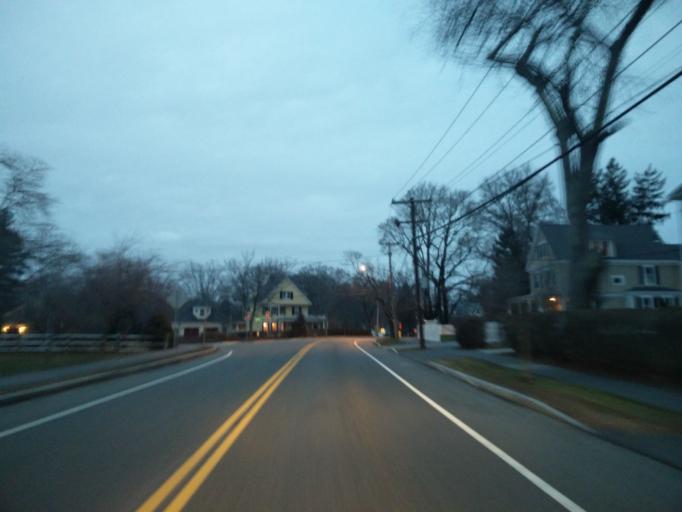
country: US
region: Massachusetts
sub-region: Plymouth County
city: Hingham
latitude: 42.2358
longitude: -70.8757
